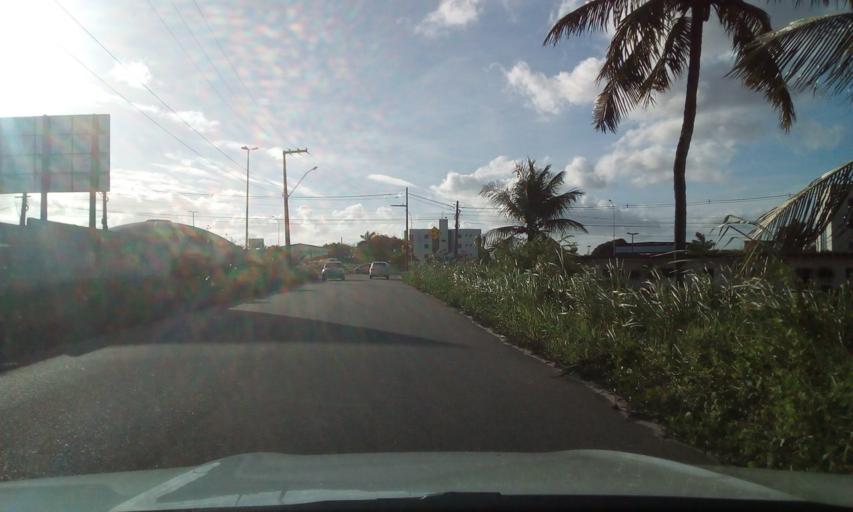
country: BR
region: Paraiba
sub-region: Joao Pessoa
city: Joao Pessoa
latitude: -7.1717
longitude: -34.8678
